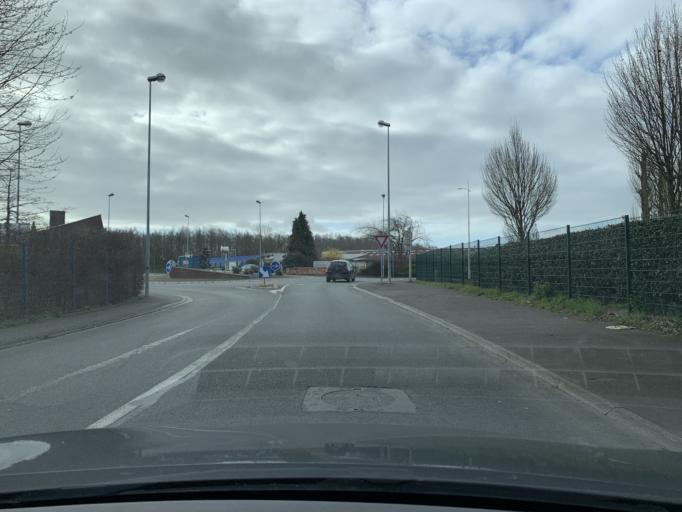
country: FR
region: Nord-Pas-de-Calais
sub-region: Departement du Nord
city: Waziers
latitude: 50.3948
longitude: 3.1027
